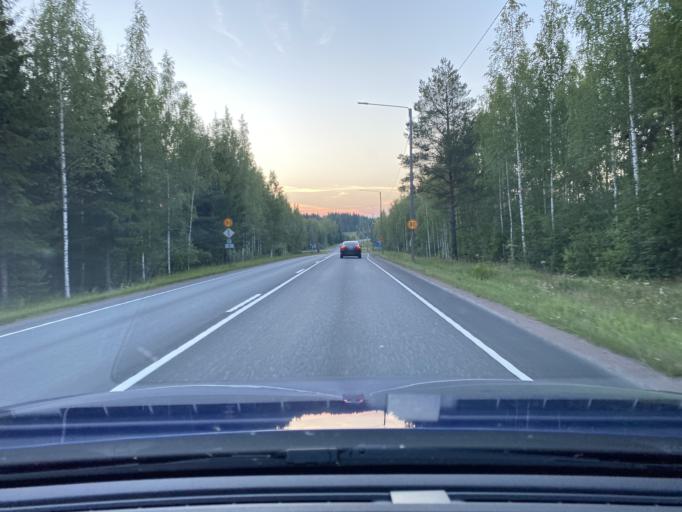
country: FI
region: Pirkanmaa
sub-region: Luoteis-Pirkanmaa
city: Ikaalinen
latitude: 61.8434
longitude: 22.9328
